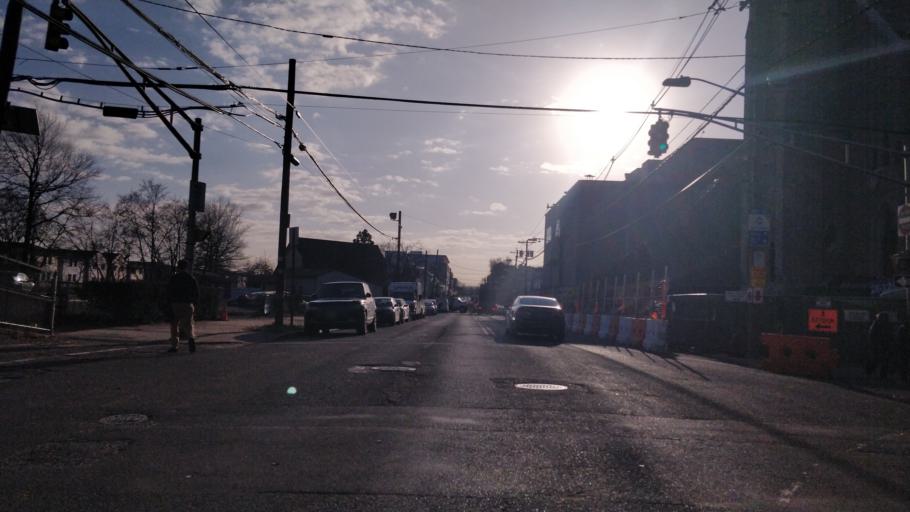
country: US
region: New Jersey
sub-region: Hudson County
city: Bayonne
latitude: 40.6646
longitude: -74.1145
